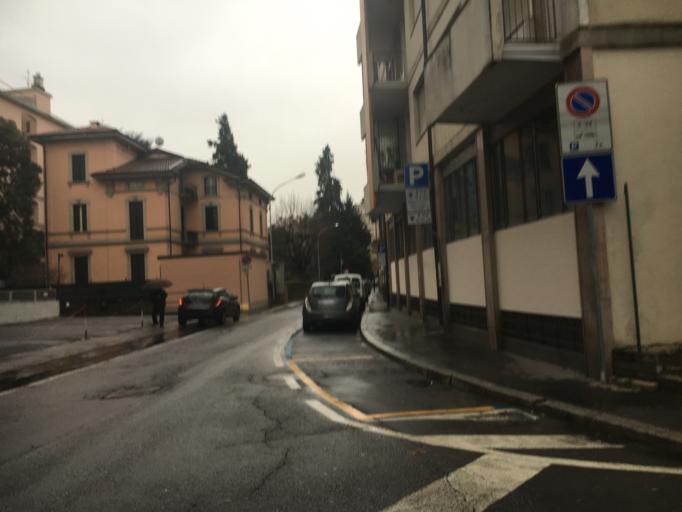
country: IT
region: Lombardy
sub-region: Provincia di Varese
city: Varese
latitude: 45.8205
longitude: 8.8289
